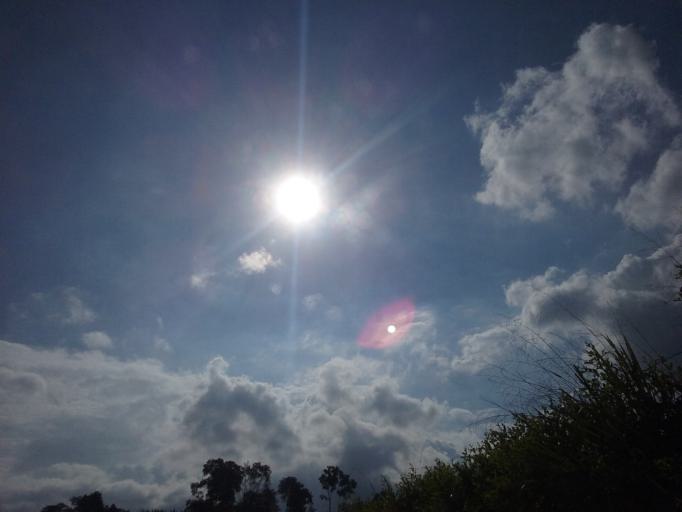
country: CO
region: Tolima
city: Libano
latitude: 4.8814
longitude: -75.0176
